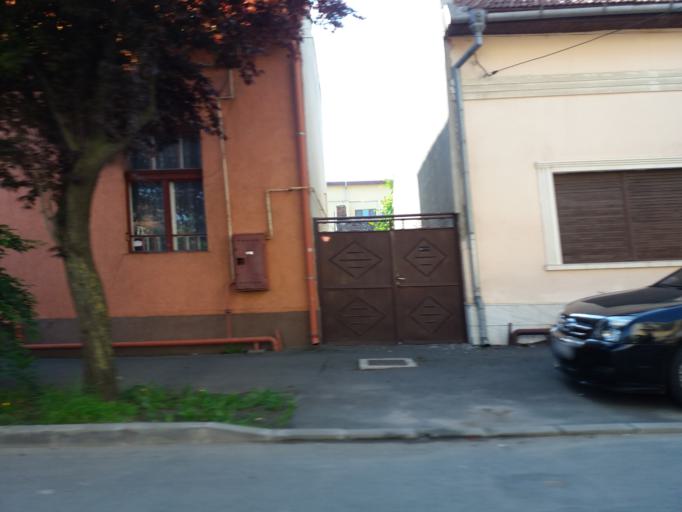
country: RO
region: Arad
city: Arad
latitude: 46.1720
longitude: 21.3047
